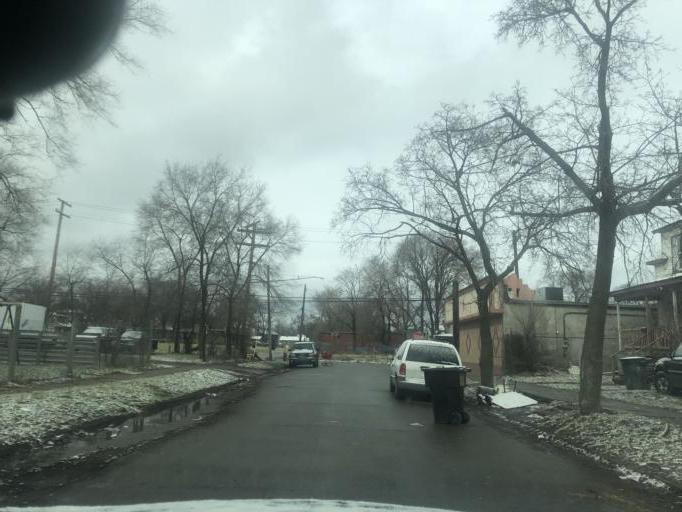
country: US
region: Michigan
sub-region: Wayne County
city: River Rouge
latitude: 42.3108
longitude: -83.1087
